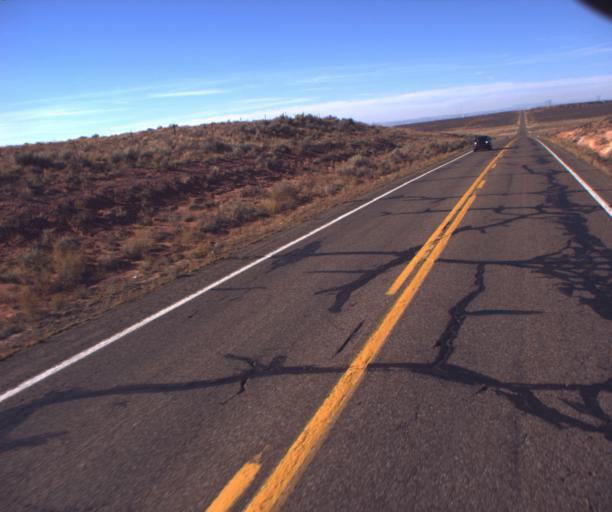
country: US
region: Arizona
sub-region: Coconino County
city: LeChee
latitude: 36.7789
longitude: -111.2888
